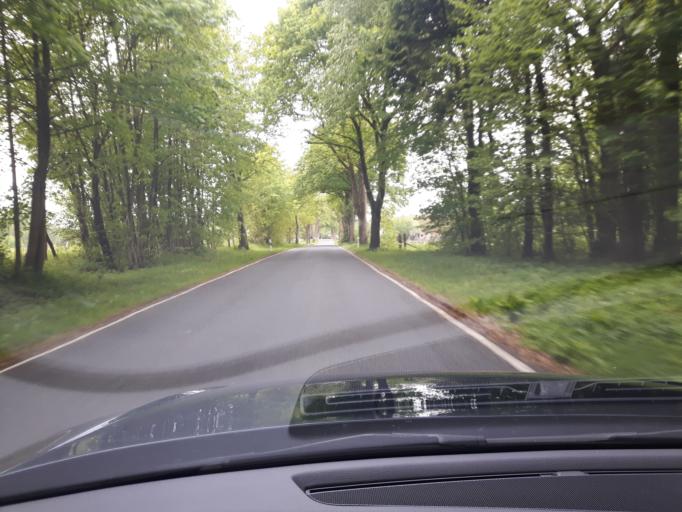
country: DE
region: Mecklenburg-Vorpommern
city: Tribsees
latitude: 54.1996
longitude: 12.7314
